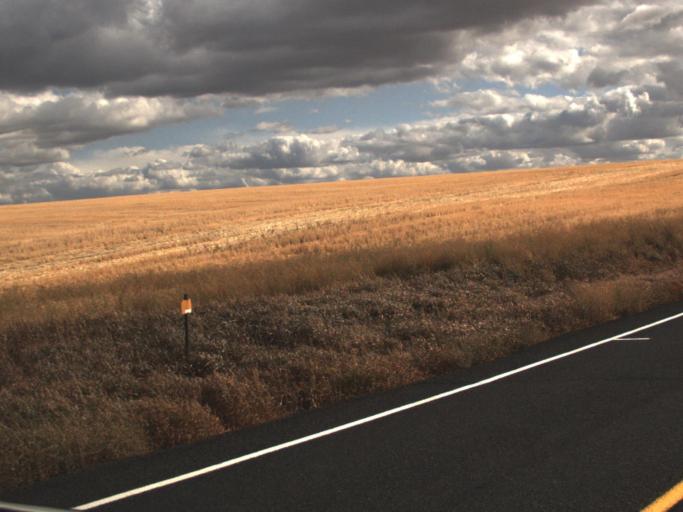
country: US
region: Washington
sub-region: Lincoln County
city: Davenport
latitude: 47.6324
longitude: -117.9375
